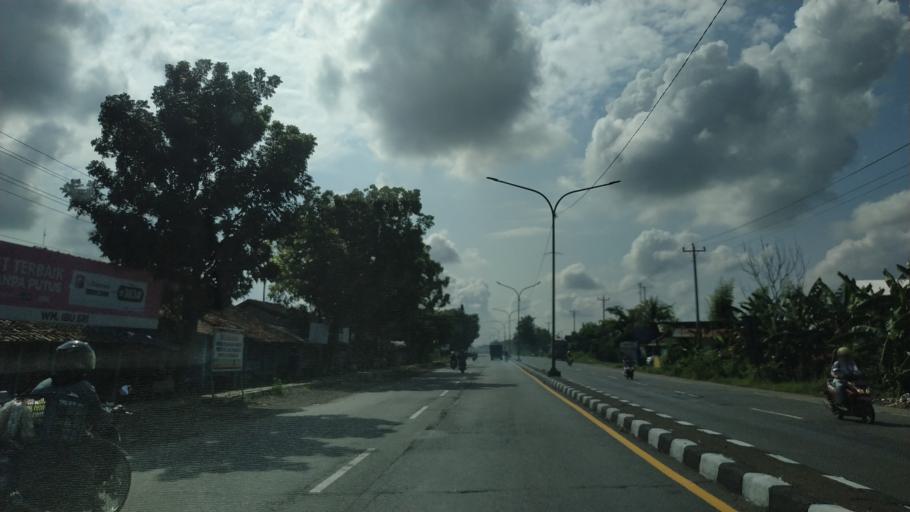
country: ID
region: Central Java
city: Comal
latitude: -6.9004
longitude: 109.5123
